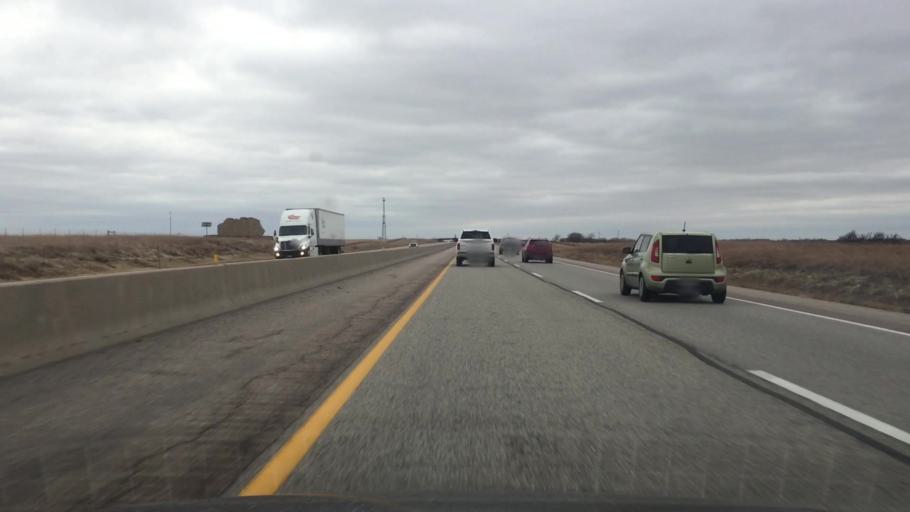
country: US
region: Kansas
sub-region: Butler County
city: El Dorado
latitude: 37.9684
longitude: -96.7242
